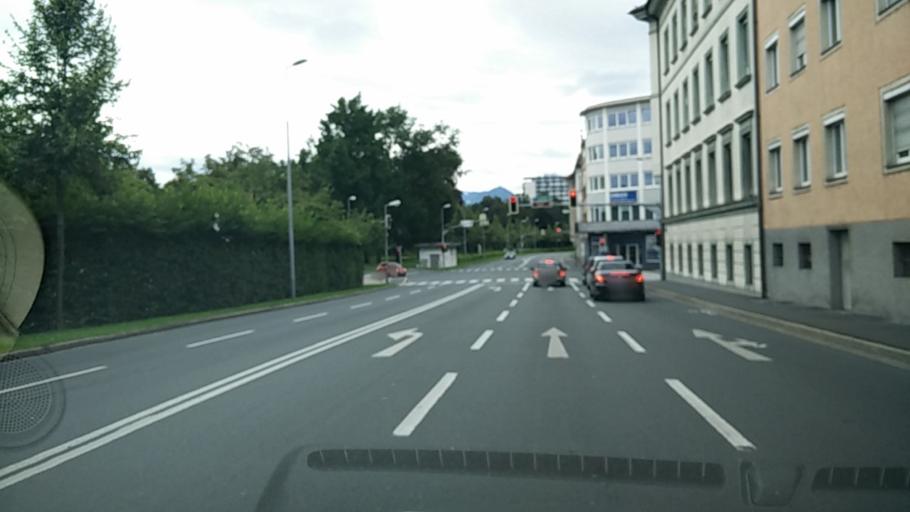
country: AT
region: Carinthia
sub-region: Klagenfurt am Woerthersee
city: Klagenfurt am Woerthersee
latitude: 46.6276
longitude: 14.3019
